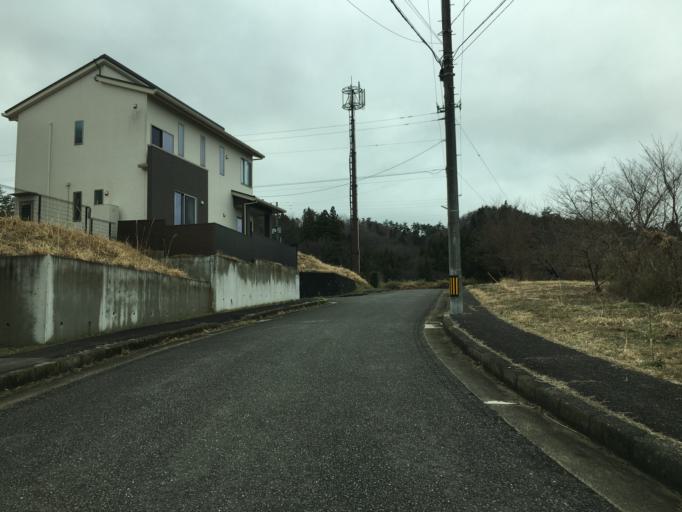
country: JP
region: Fukushima
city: Fukushima-shi
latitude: 37.7180
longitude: 140.4055
